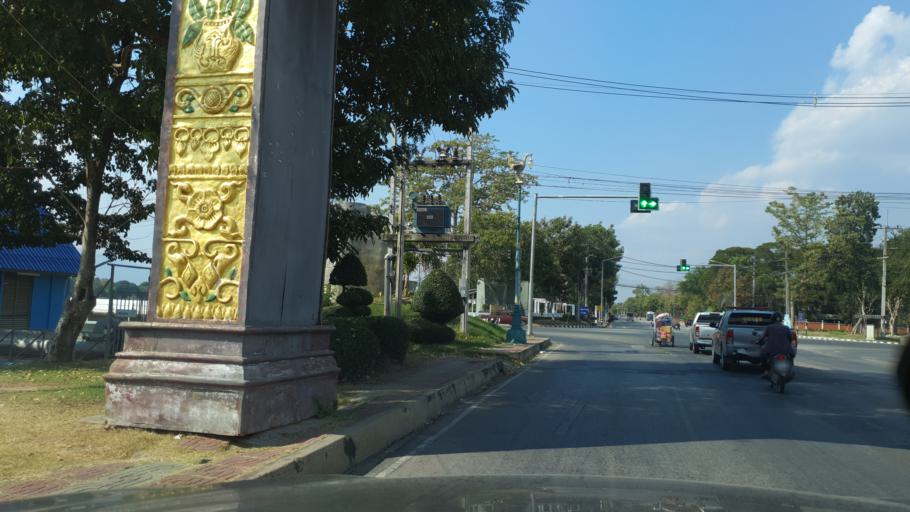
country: TH
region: Tak
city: Tak
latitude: 16.8835
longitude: 99.1179
